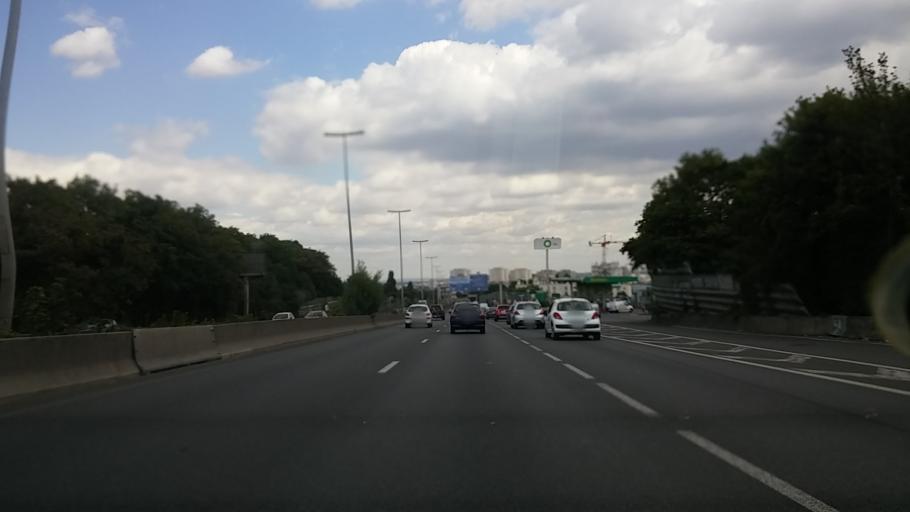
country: FR
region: Ile-de-France
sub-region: Departement de Seine-Saint-Denis
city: Romainville
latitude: 48.8800
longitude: 2.4502
